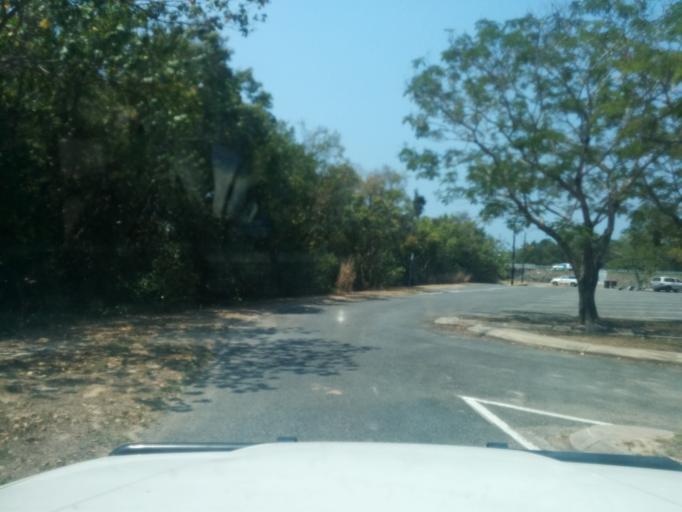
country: AU
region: Queensland
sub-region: Cairns
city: Redlynch
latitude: -16.8707
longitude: 145.7364
